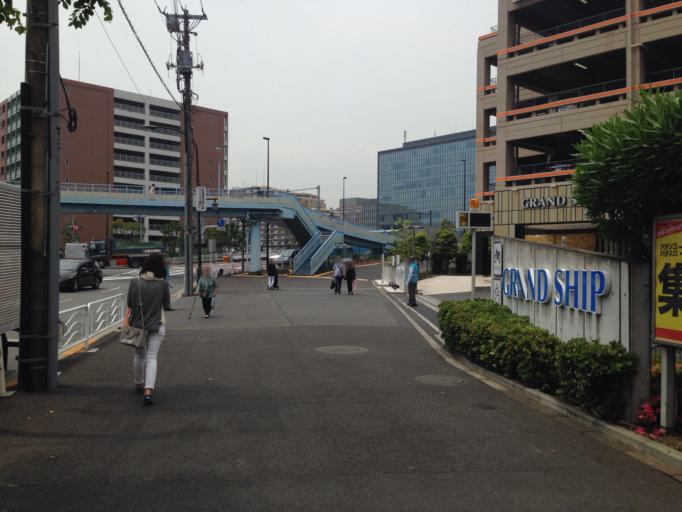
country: JP
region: Tokyo
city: Urayasu
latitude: 35.6499
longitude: 139.8021
